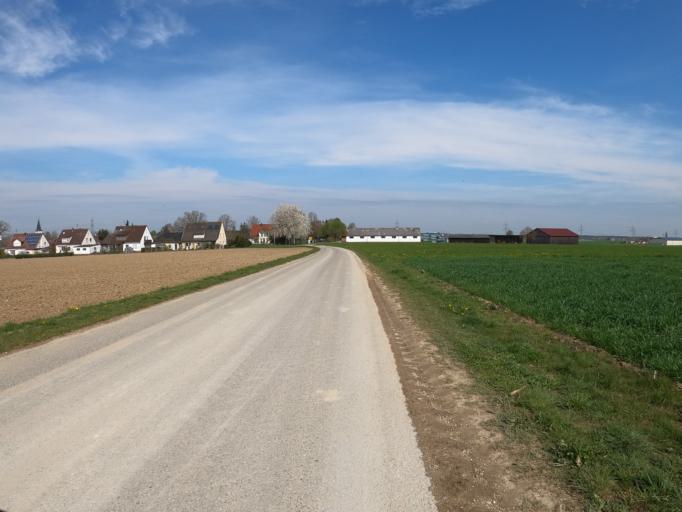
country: DE
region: Bavaria
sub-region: Swabia
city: Rieden an der Kotz
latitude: 48.3813
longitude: 10.2183
